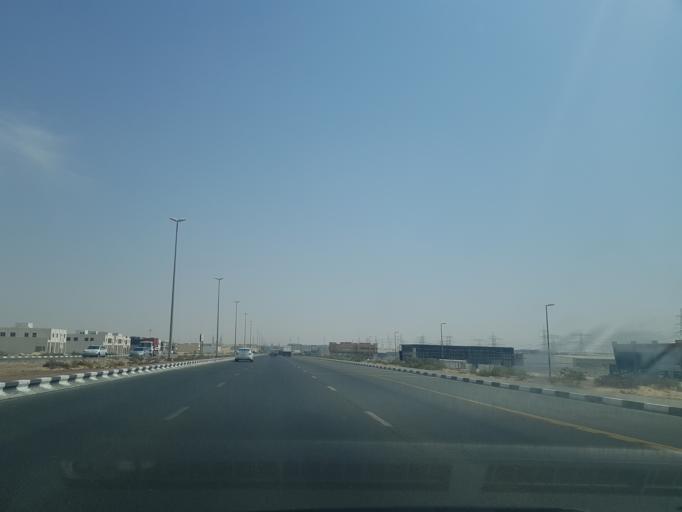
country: AE
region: Ash Shariqah
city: Sharjah
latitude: 25.2517
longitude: 55.5309
